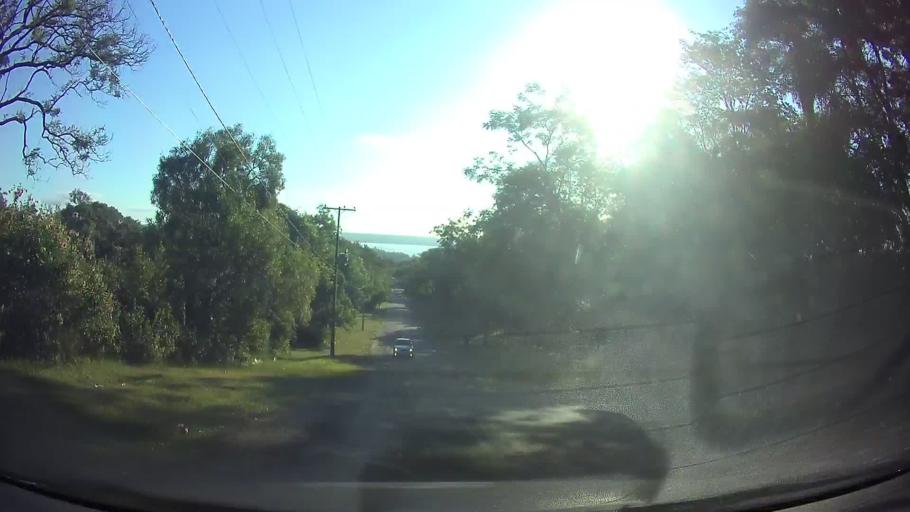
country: PY
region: Cordillera
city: San Bernardino
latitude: -25.3173
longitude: -57.2685
